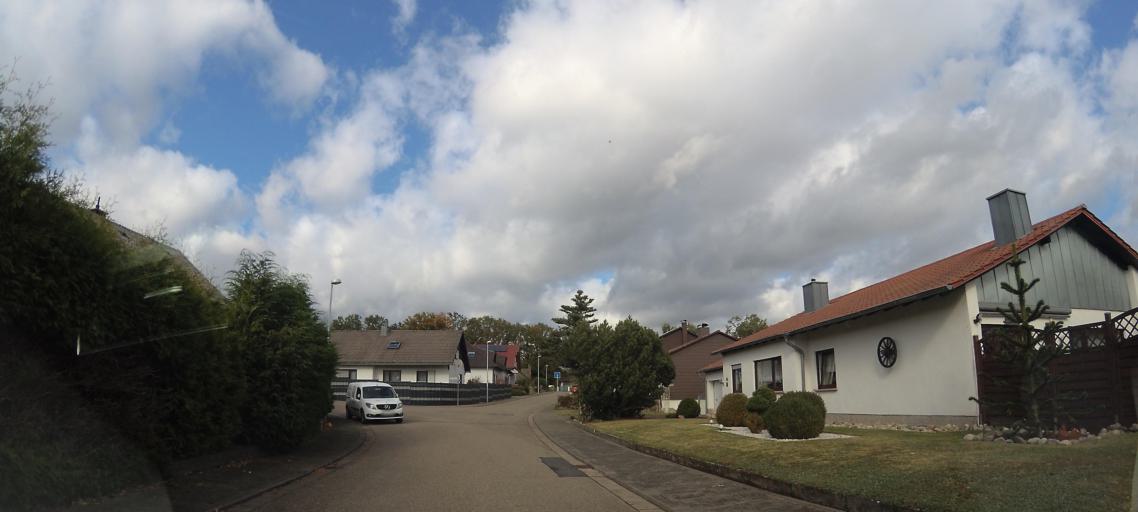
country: DE
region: Saarland
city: Blieskastel
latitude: 49.2569
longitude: 7.2505
